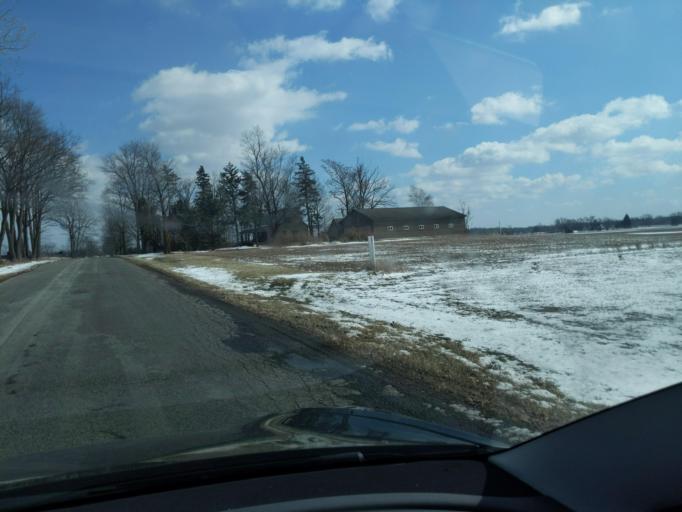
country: US
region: Michigan
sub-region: Ingham County
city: Webberville
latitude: 42.6145
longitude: -84.1656
